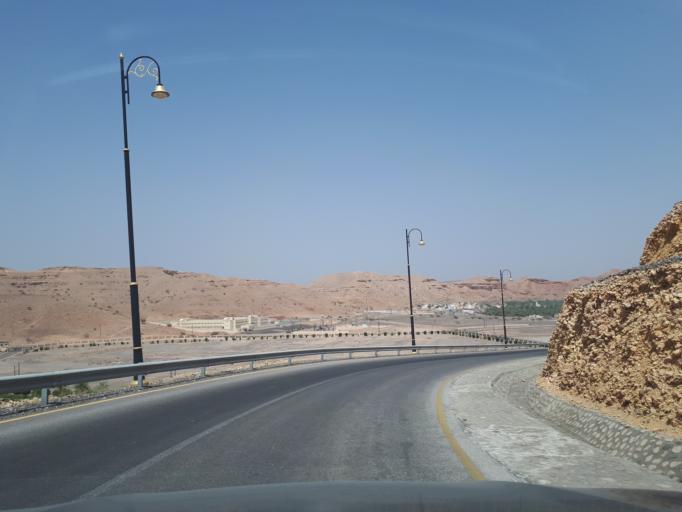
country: OM
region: Ash Sharqiyah
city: Ibra'
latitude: 23.0900
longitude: 58.8493
